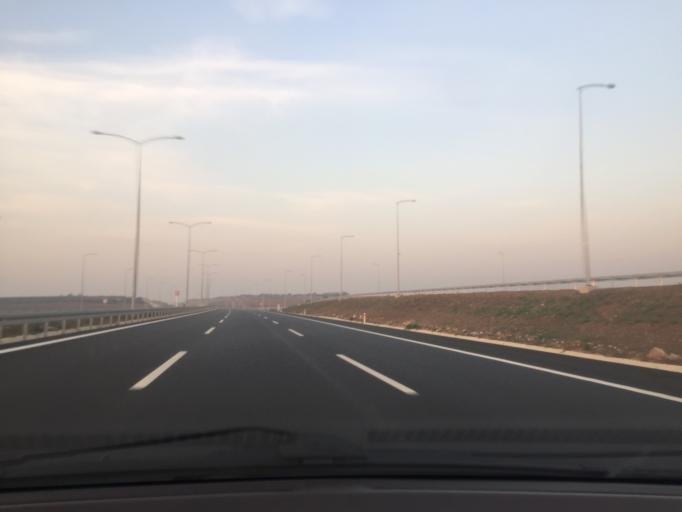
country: TR
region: Bursa
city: Karacabey
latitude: 40.2508
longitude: 28.4489
